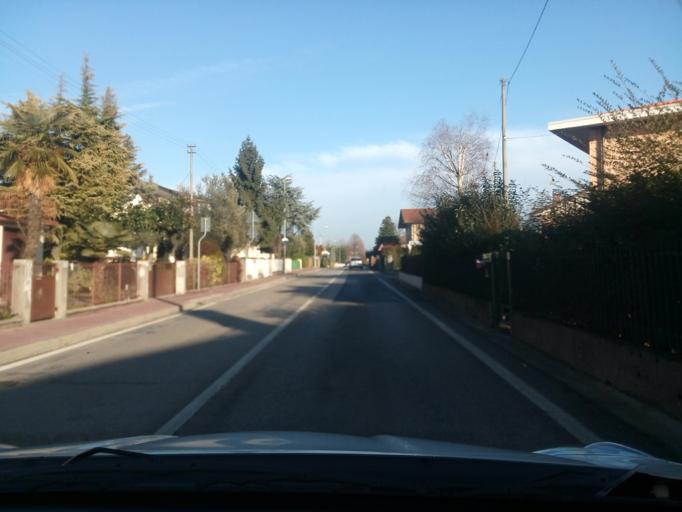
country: IT
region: Veneto
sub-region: Provincia di Vicenza
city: Dueville
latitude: 45.6404
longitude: 11.5538
